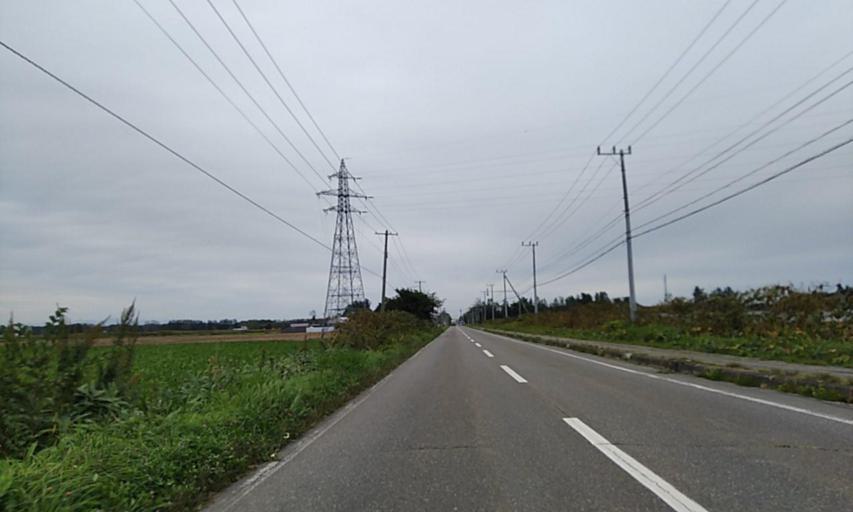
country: JP
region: Hokkaido
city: Obihiro
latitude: 42.6825
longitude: 143.1216
